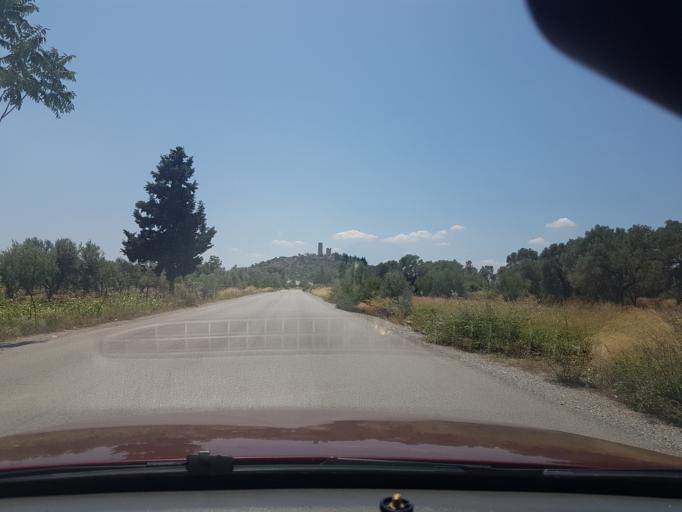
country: GR
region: Central Greece
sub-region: Nomos Evvoias
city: Filla
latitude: 38.4506
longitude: 23.6760
